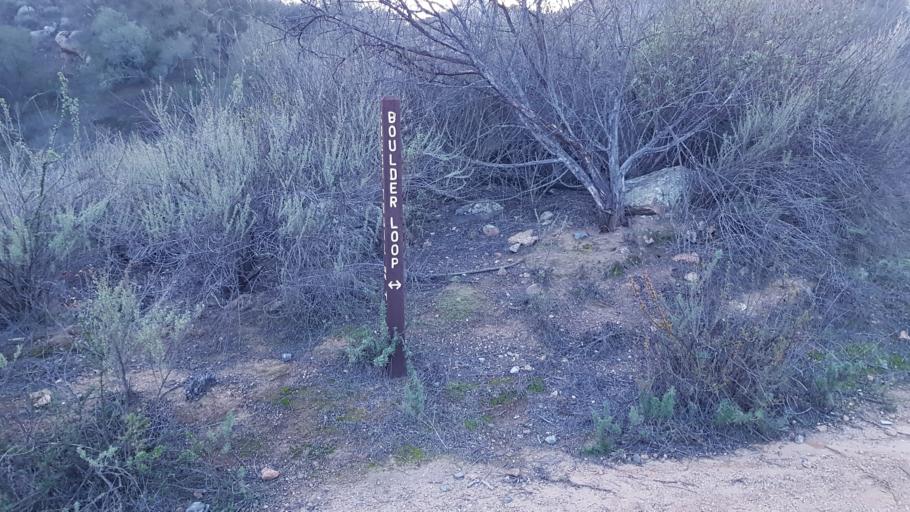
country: US
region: California
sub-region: San Diego County
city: Valley Center
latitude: 33.1755
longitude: -117.0523
